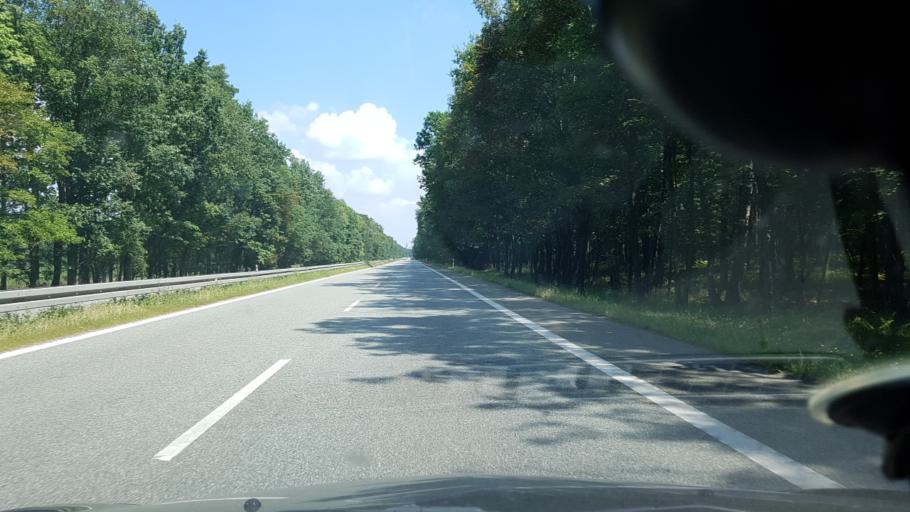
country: PL
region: Silesian Voivodeship
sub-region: Zory
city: Zory
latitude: 50.0668
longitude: 18.7306
